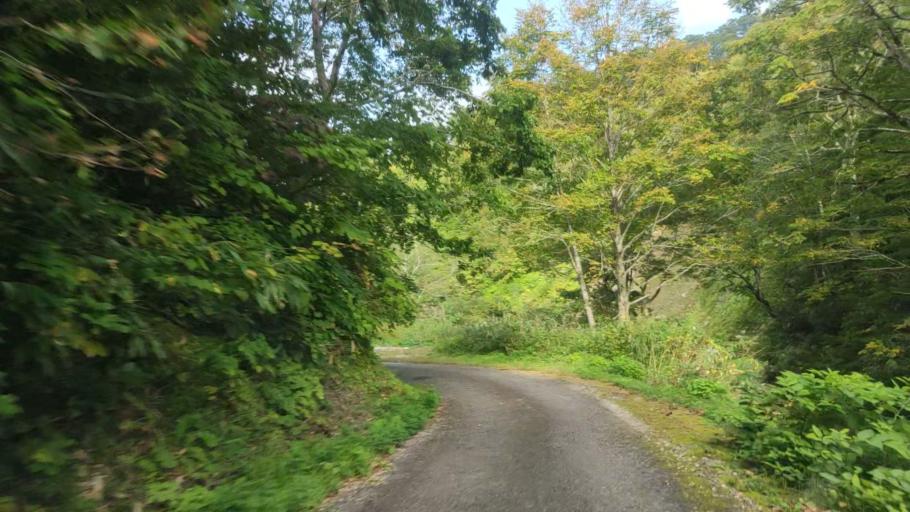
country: JP
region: Toyama
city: Yatsuomachi-higashikumisaka
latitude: 36.3640
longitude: 137.0718
